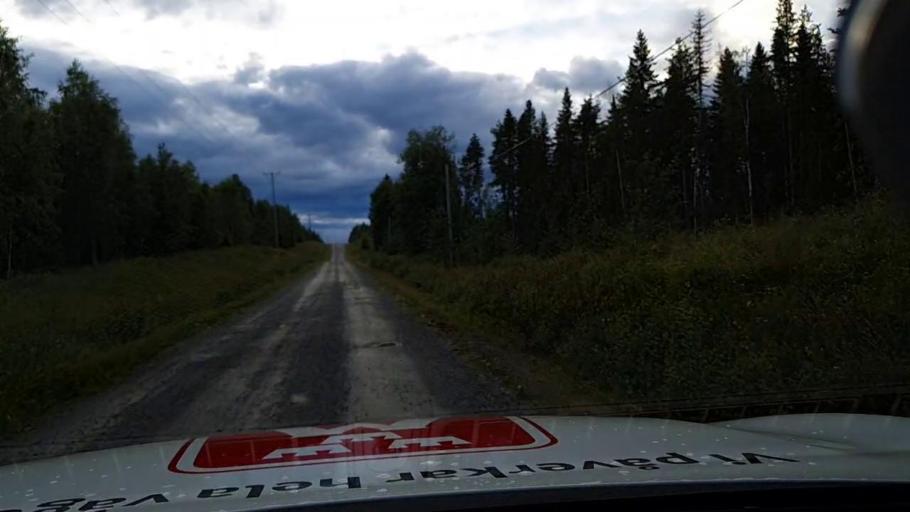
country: SE
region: Jaemtland
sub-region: Bergs Kommun
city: Hoverberg
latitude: 62.8880
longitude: 14.5739
